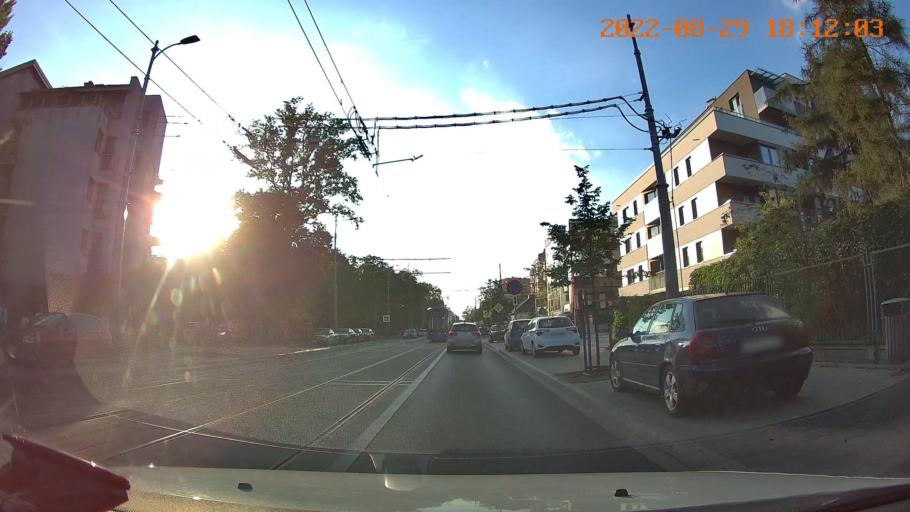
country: PL
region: Lesser Poland Voivodeship
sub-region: Krakow
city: Krakow
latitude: 50.0761
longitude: 19.9054
